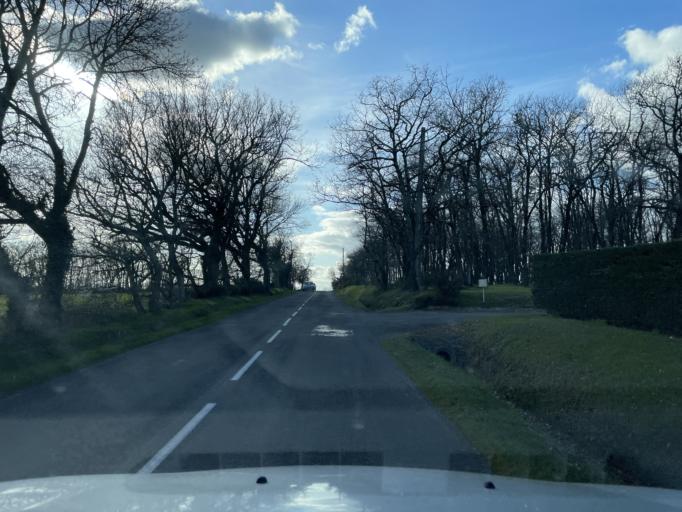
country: FR
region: Midi-Pyrenees
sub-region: Departement du Gers
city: Pujaudran
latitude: 43.6203
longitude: 1.1815
